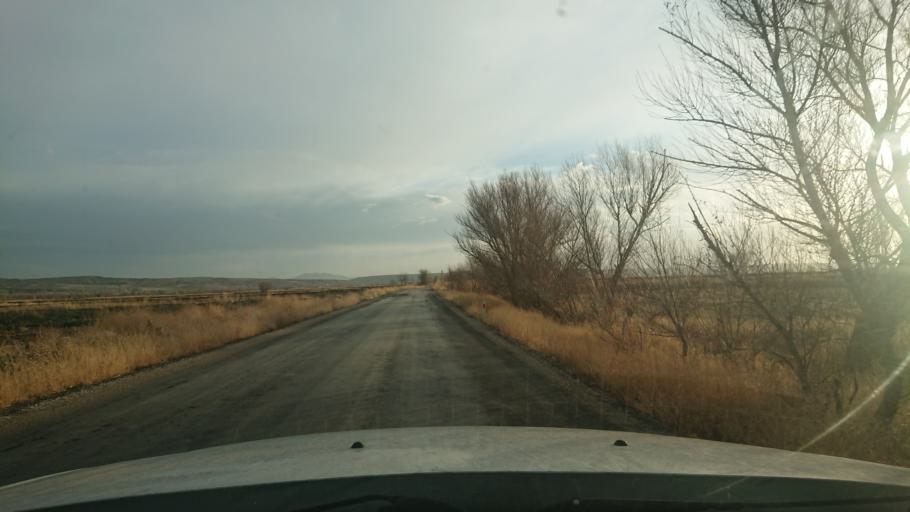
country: TR
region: Aksaray
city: Acipinar
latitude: 38.4761
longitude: 33.8681
